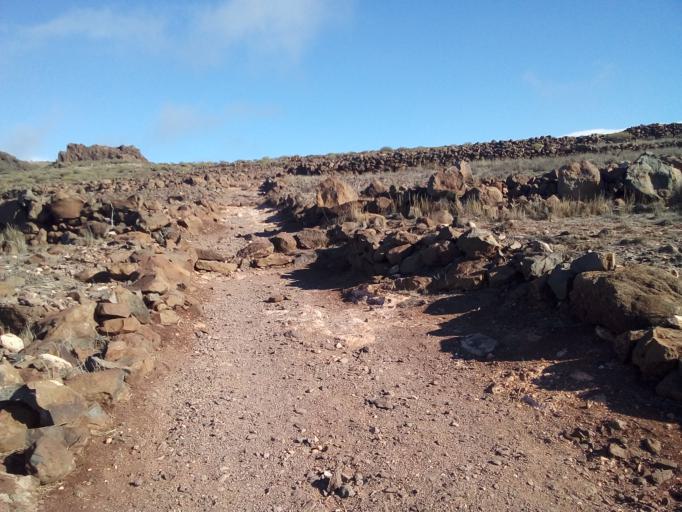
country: ES
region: Canary Islands
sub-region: Provincia de Santa Cruz de Tenerife
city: Vallehermosa
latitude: 28.1098
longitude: -17.3359
